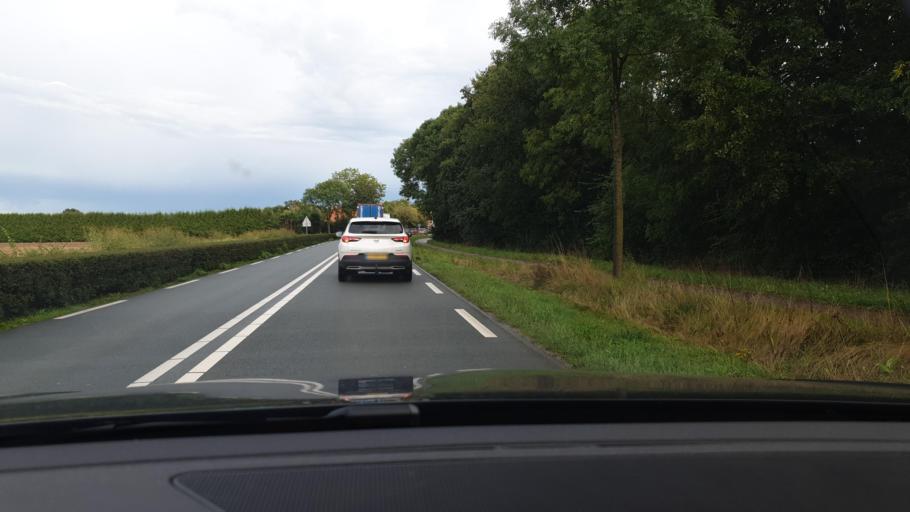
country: NL
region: North Brabant
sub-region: Gemeente Landerd
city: Schaijk
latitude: 51.7991
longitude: 5.6369
